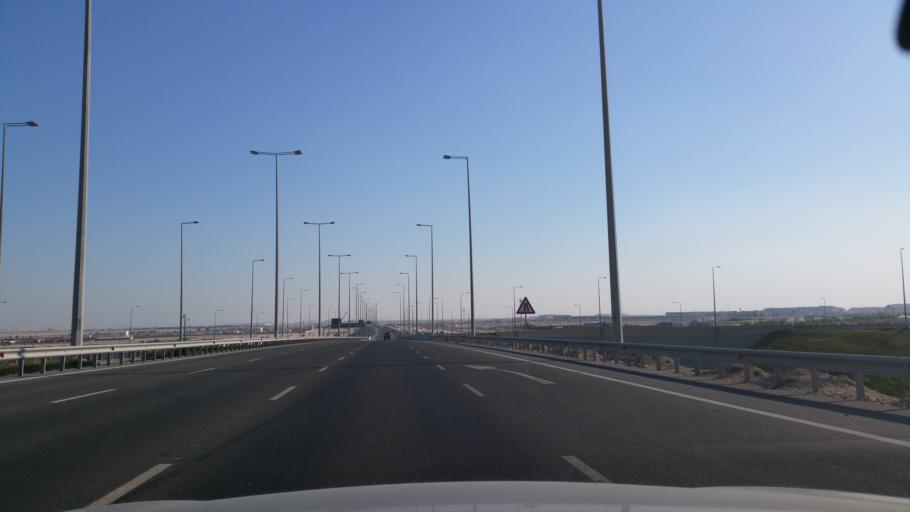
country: QA
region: Al Wakrah
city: Al Wukayr
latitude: 25.1646
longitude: 51.4718
